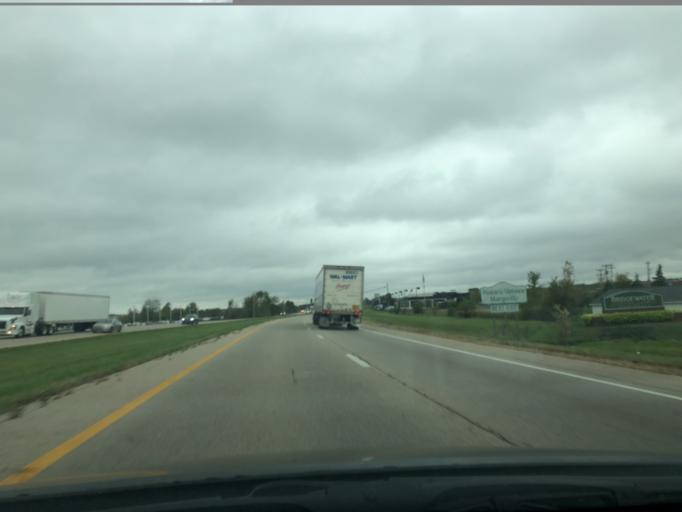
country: US
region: Ohio
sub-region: Union County
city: Marysville
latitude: 40.2324
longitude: -83.3394
